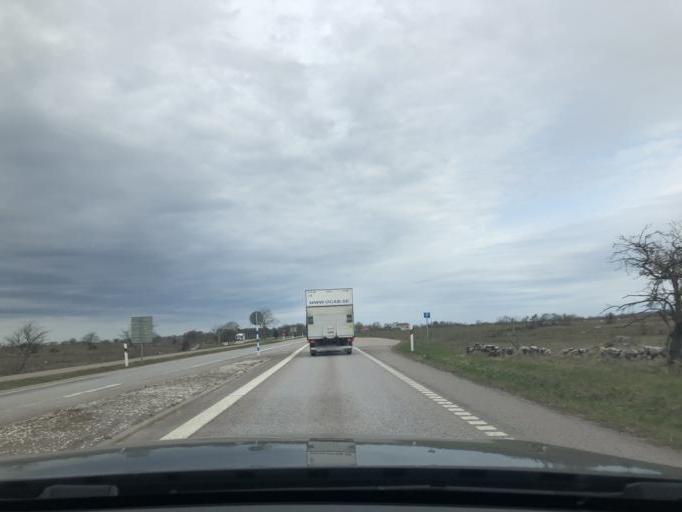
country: SE
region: Kalmar
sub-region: Borgholms Kommun
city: Borgholm
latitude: 56.8609
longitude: 16.6514
